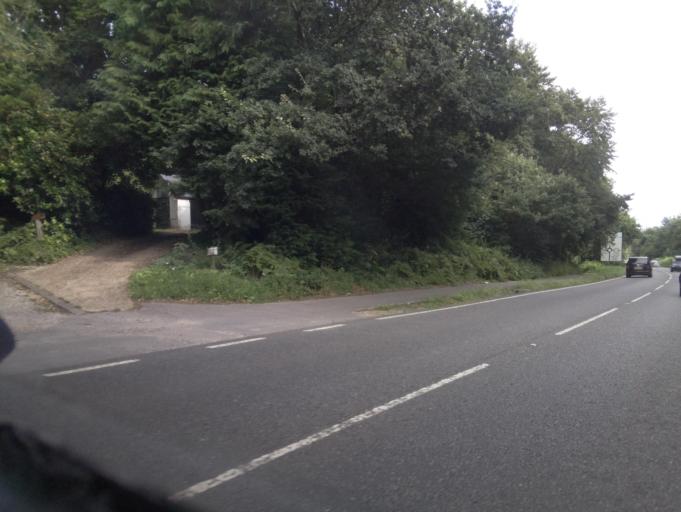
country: GB
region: England
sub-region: Hampshire
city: Marchwood
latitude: 50.8661
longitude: -1.4376
